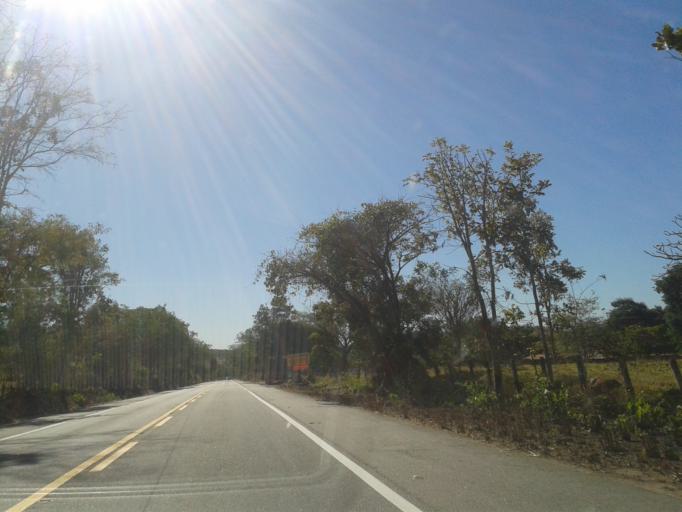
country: BR
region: Goias
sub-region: Goias
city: Goias
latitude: -15.7987
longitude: -50.1253
